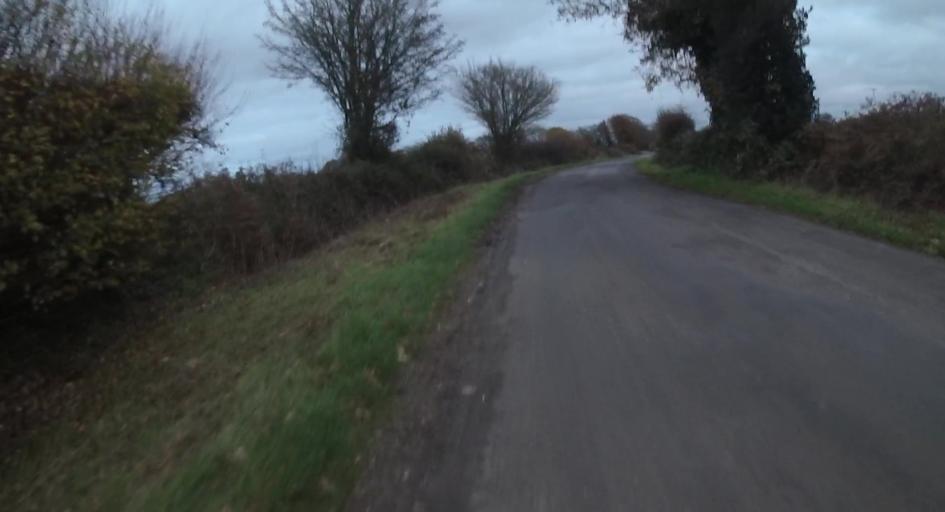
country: GB
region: England
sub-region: Hampshire
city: Long Sutton
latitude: 51.2182
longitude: -0.9000
